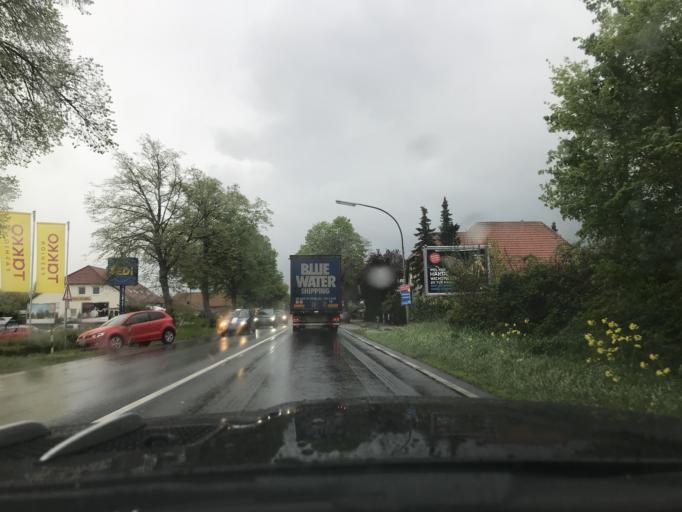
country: DE
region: Lower Saxony
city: Meine
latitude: 52.3827
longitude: 10.5335
